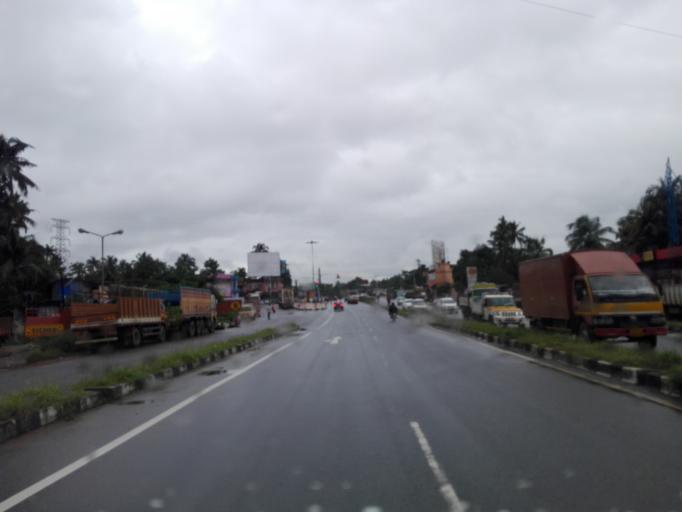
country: IN
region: Kerala
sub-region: Ernakulam
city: Elur
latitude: 10.0689
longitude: 76.3218
